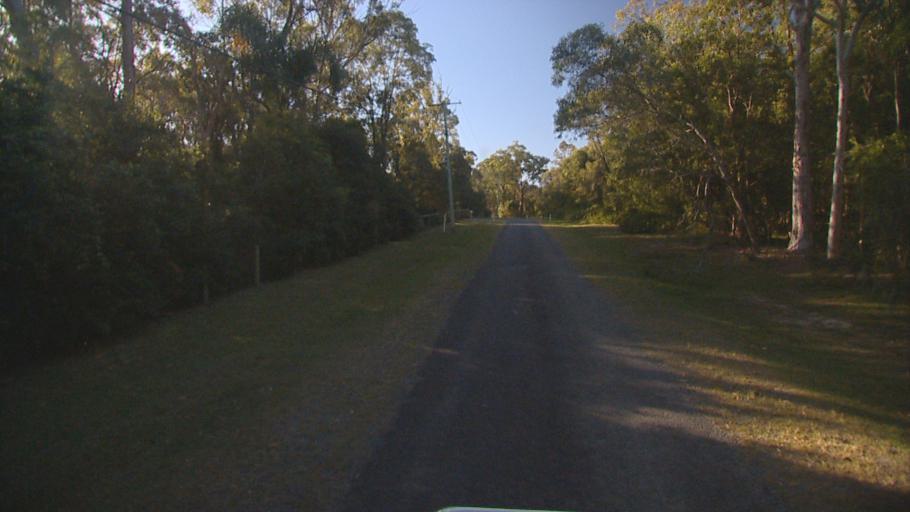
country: AU
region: Queensland
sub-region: Gold Coast
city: Yatala
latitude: -27.6633
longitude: 153.2453
